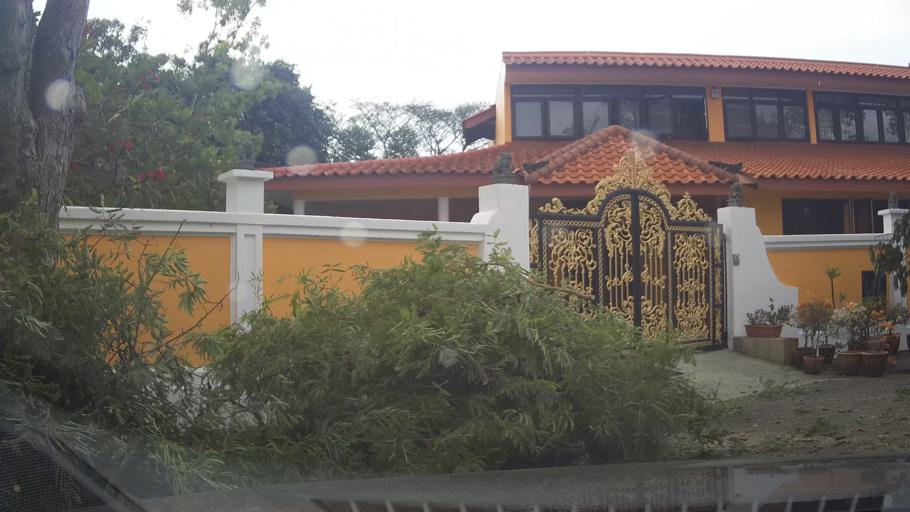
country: SG
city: Singapore
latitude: 1.2979
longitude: 103.8971
